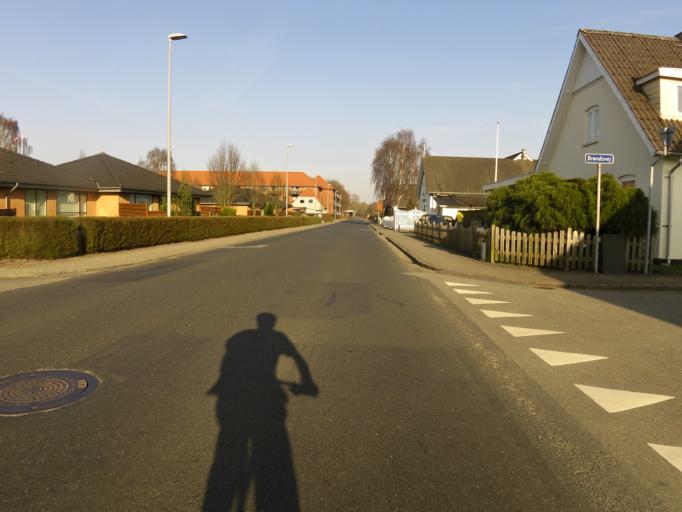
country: DK
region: South Denmark
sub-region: Vejen Kommune
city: Vejen
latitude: 55.4729
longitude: 9.1381
